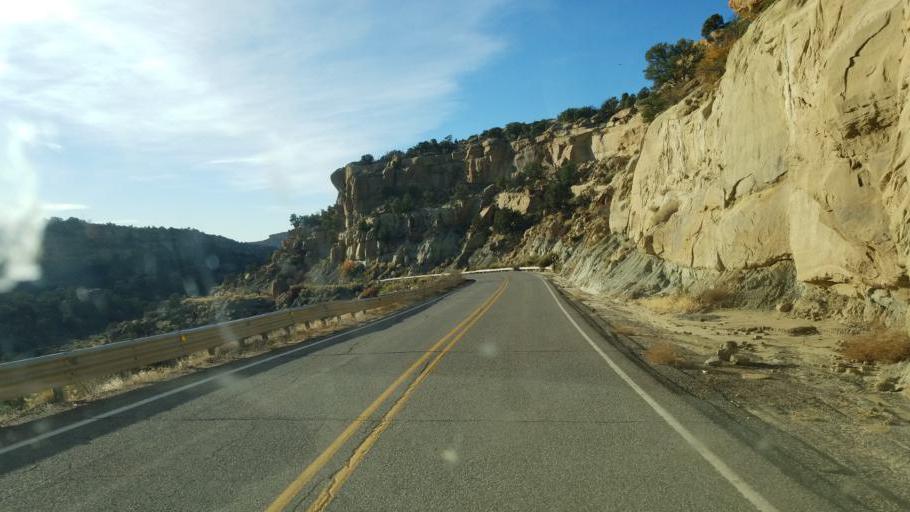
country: US
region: New Mexico
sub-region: San Juan County
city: Bloomfield
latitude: 36.7365
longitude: -107.7020
